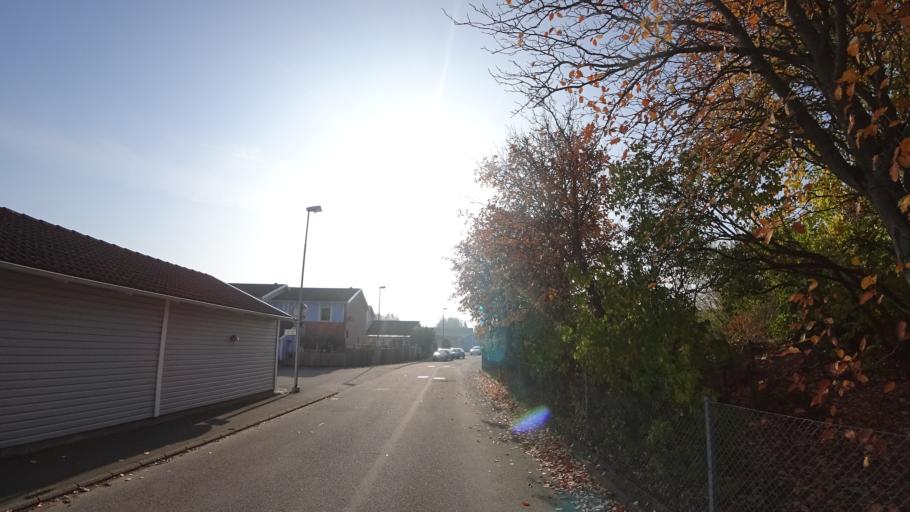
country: SE
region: Skane
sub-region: Staffanstorps Kommun
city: Staffanstorp
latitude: 55.6519
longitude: 13.2185
